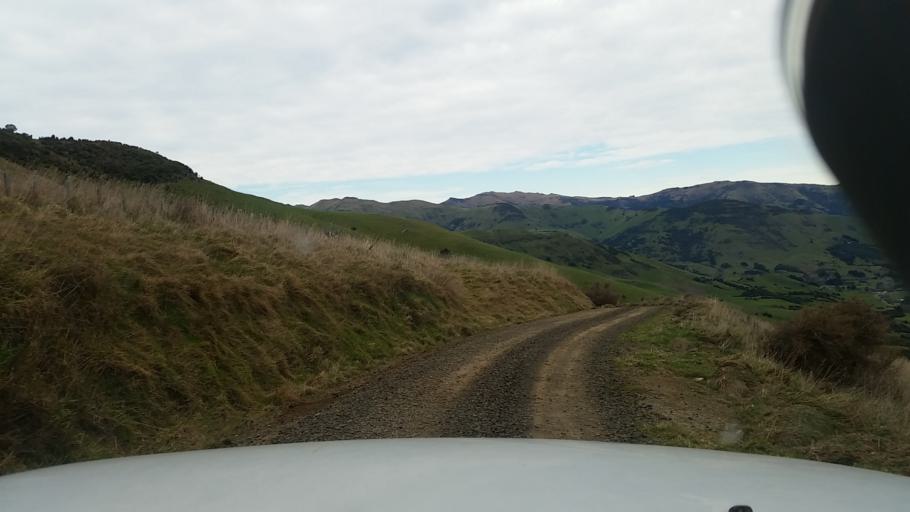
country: NZ
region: Canterbury
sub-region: Christchurch City
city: Christchurch
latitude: -43.7217
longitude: 172.7963
